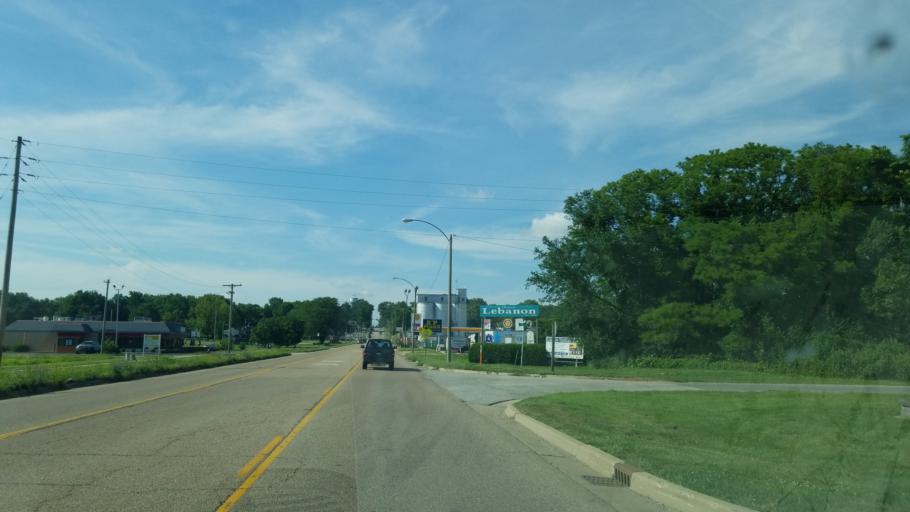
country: US
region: Illinois
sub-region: Saint Clair County
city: Lebanon
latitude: 38.5975
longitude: -89.8076
